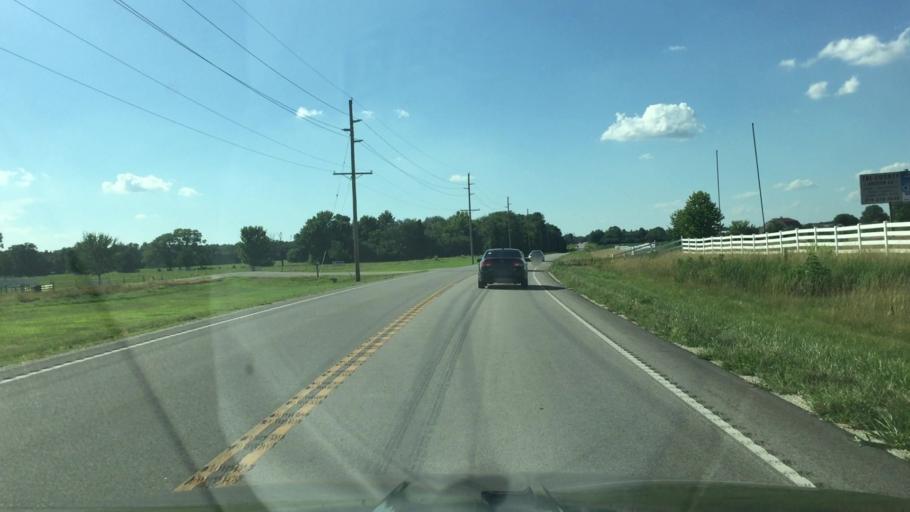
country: US
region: Missouri
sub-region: Morgan County
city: Versailles
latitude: 38.4074
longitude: -92.7632
